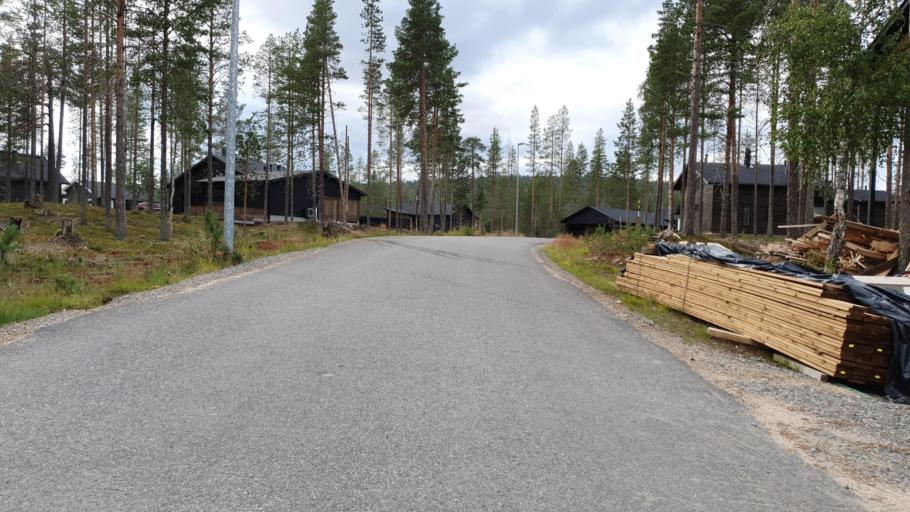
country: FI
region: Lapland
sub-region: Tunturi-Lappi
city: Kolari
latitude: 67.5948
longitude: 24.1278
